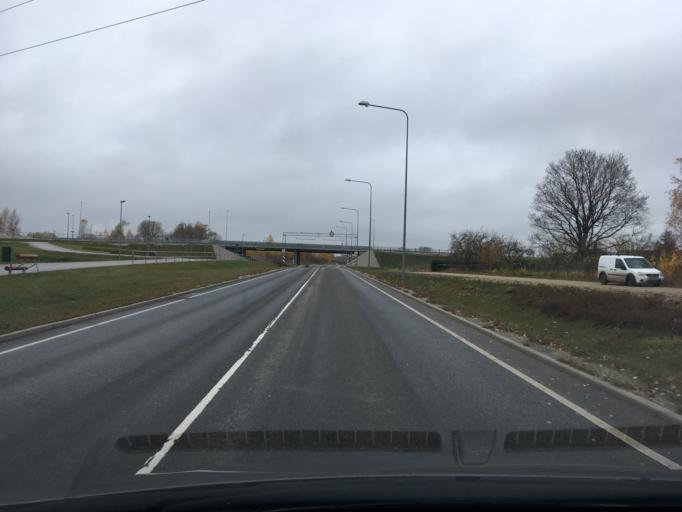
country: EE
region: Tartu
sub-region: Tartu linn
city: Tartu
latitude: 58.3544
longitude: 26.7655
